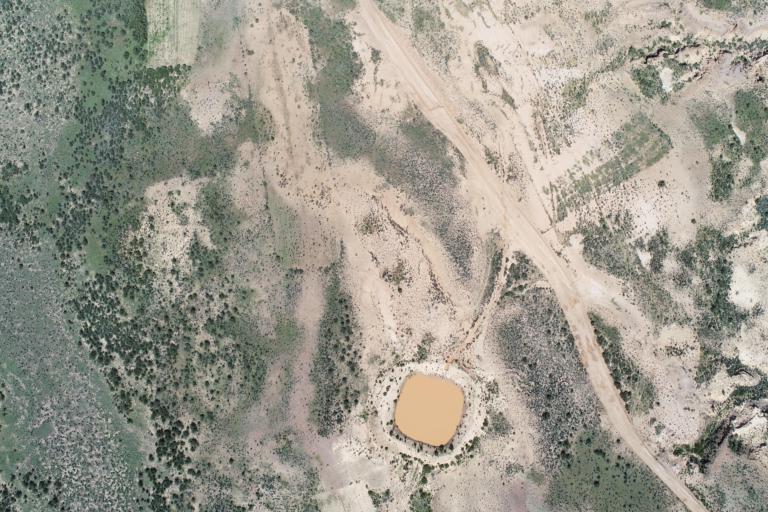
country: BO
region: La Paz
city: Curahuara de Carangas
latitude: -17.2944
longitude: -68.5143
